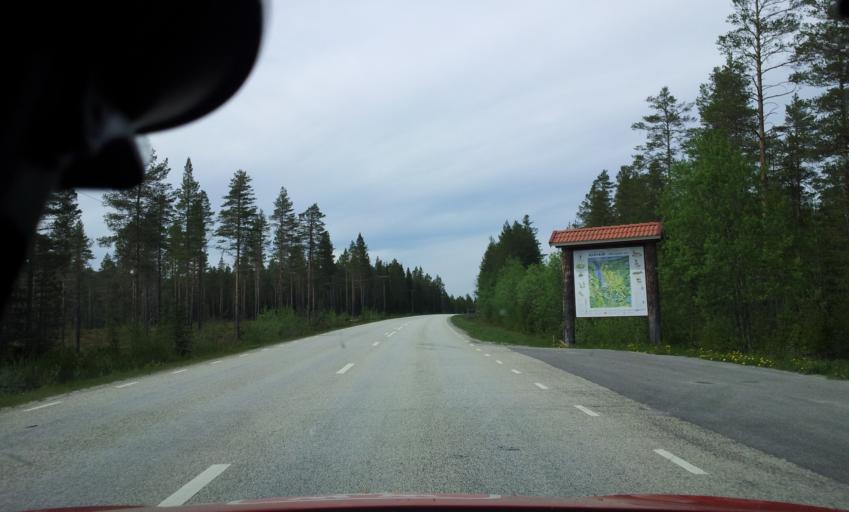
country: SE
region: Jaemtland
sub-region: Bergs Kommun
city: Hoverberg
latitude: 62.5020
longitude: 14.2027
